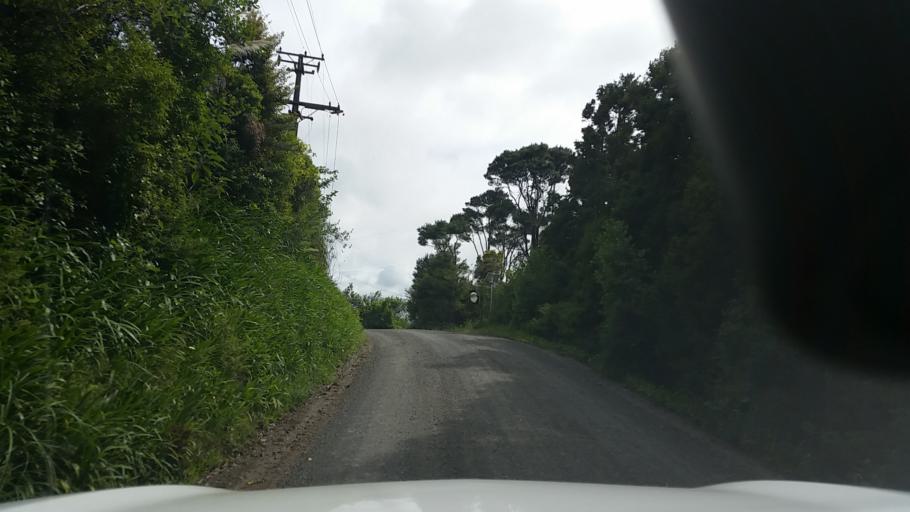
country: NZ
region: Auckland
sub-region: Auckland
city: Muriwai Beach
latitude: -36.8488
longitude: 174.5229
